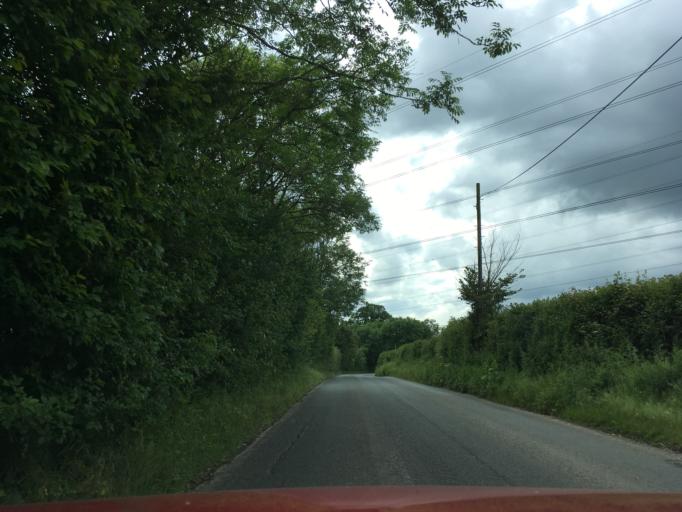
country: GB
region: England
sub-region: Wiltshire
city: Minety
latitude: 51.6451
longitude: -1.9956
